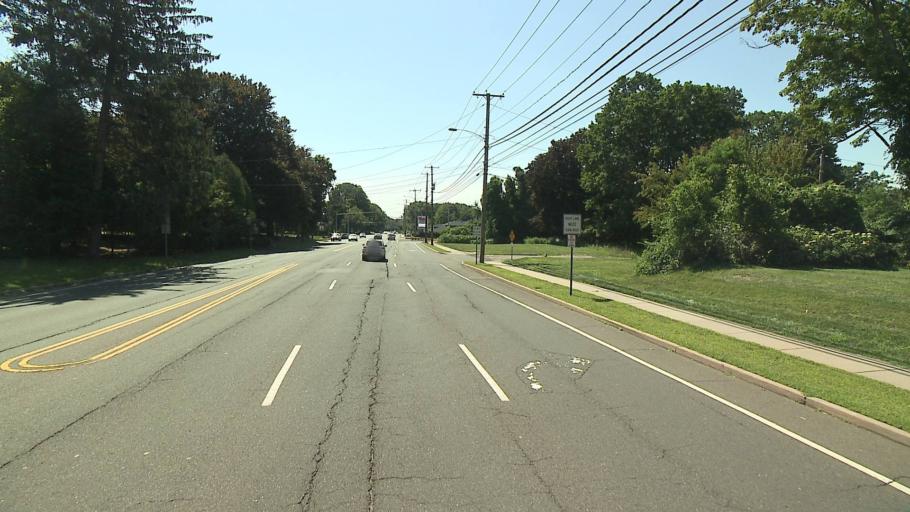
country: US
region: Connecticut
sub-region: Fairfield County
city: Trumbull
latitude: 41.2307
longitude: -73.2202
